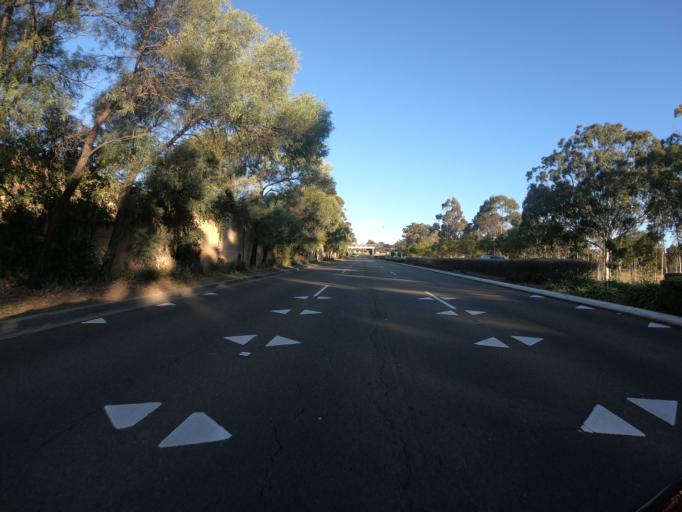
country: AU
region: New South Wales
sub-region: Campbelltown Municipality
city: Campbelltown
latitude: -34.0591
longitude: 150.8246
